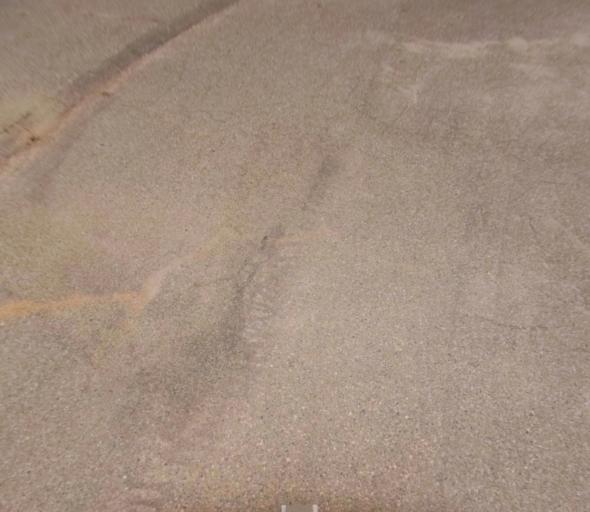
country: US
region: California
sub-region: Madera County
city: Oakhurst
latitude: 37.3275
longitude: -119.6221
